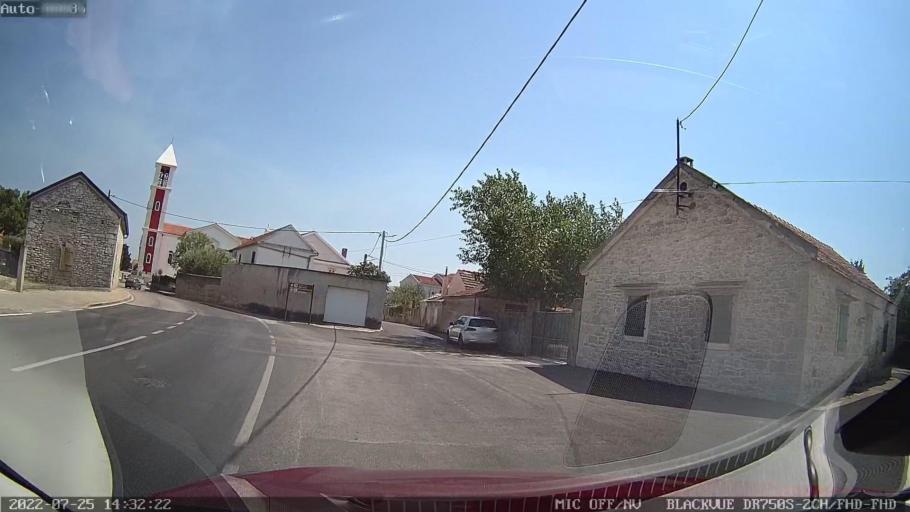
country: HR
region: Zadarska
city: Galovac
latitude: 44.1060
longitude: 15.3789
